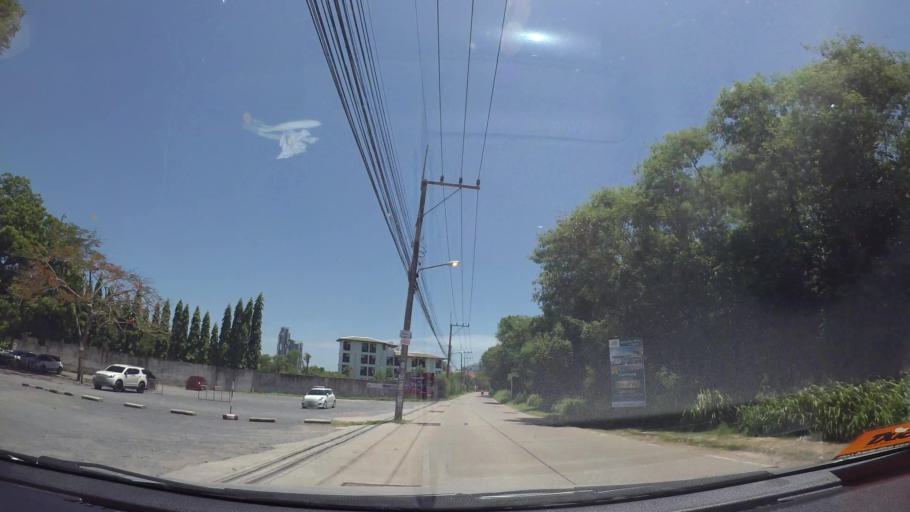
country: TH
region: Chon Buri
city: Phatthaya
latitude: 12.9429
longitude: 100.8999
